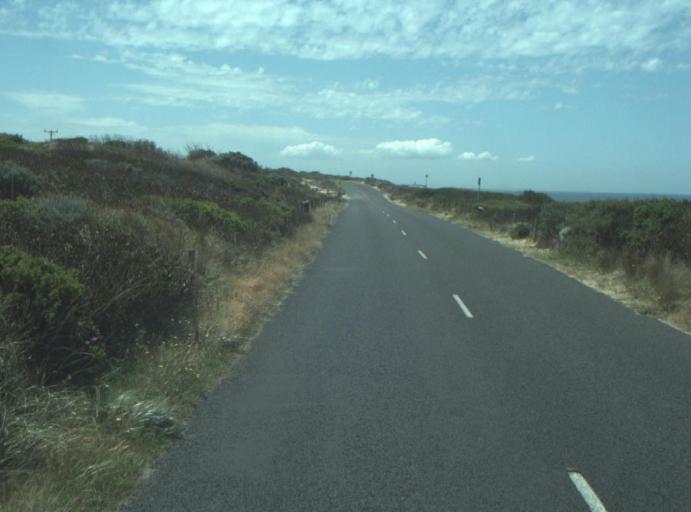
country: AU
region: Victoria
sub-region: Greater Geelong
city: Leopold
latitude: -38.2861
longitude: 144.4684
